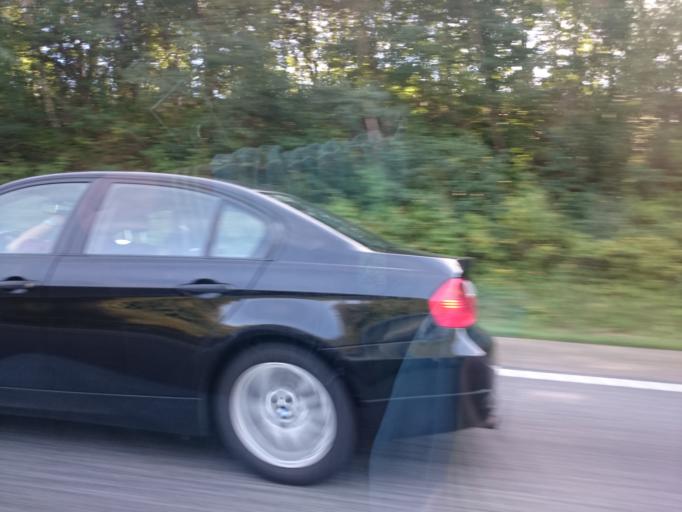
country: DK
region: Central Jutland
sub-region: Skanderborg Kommune
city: Skanderborg
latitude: 56.0510
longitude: 9.9318
